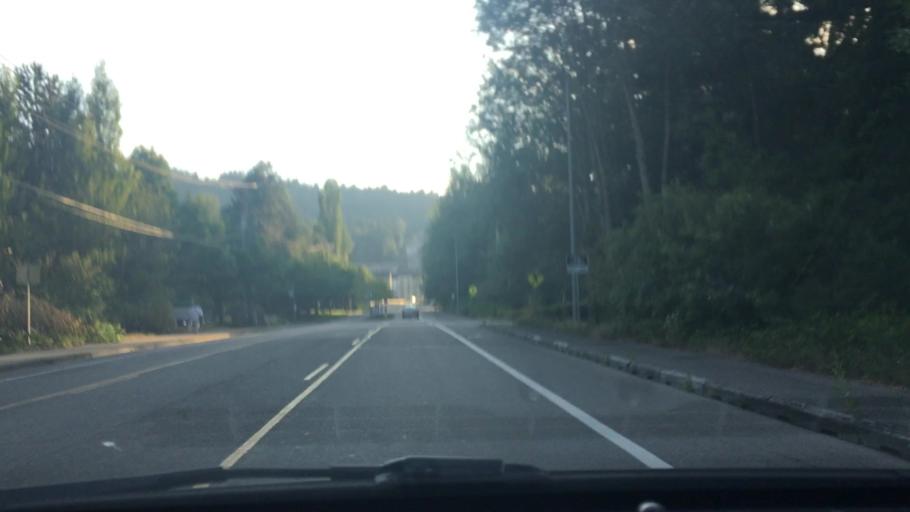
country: US
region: Washington
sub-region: King County
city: Issaquah
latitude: 47.5520
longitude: -122.0643
